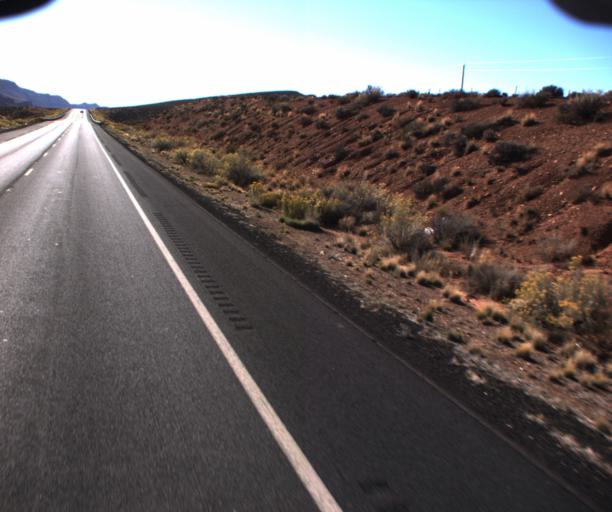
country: US
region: Arizona
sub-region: Coconino County
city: Tuba City
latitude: 36.2709
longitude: -111.4340
